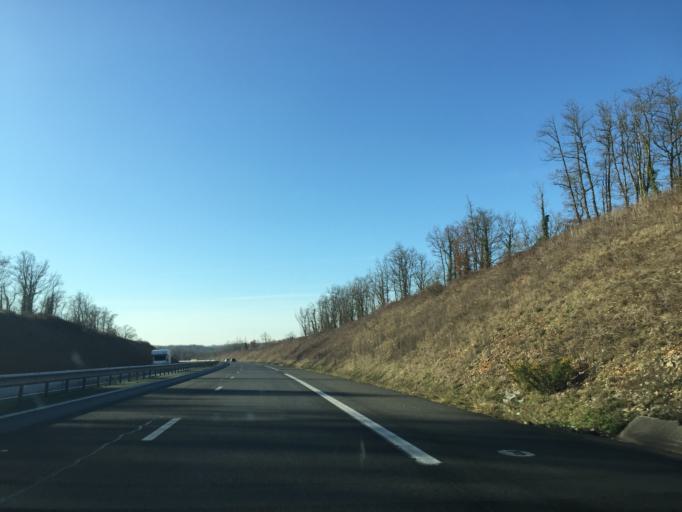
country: FR
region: Aquitaine
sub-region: Departement de la Dordogne
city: Thenon
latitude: 45.1782
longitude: 0.9797
